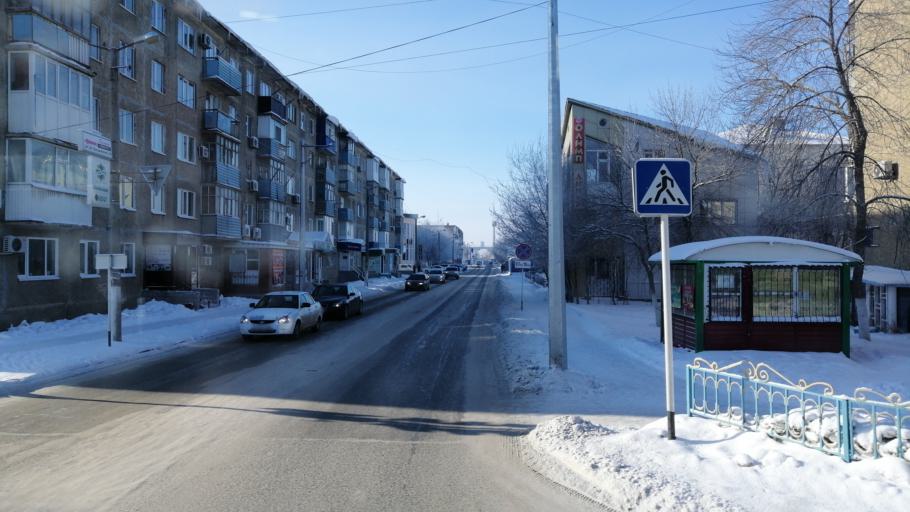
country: KZ
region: Aqtoebe
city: Aqtobe
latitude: 50.3057
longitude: 57.1505
